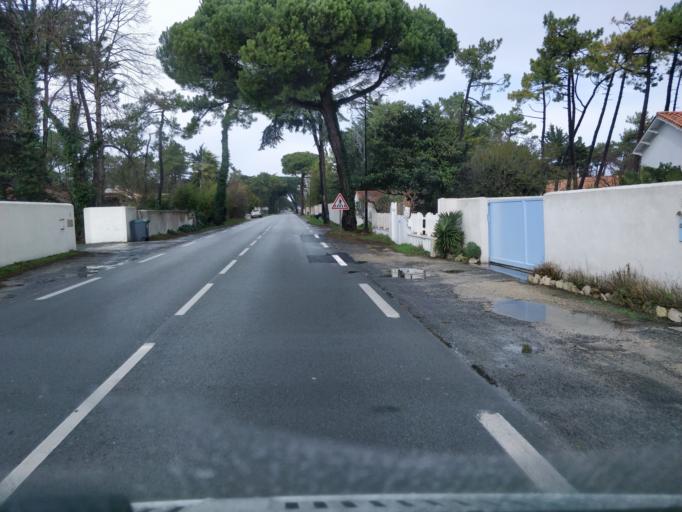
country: FR
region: Poitou-Charentes
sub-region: Departement de la Charente-Maritime
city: Rivedoux-Plage
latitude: 46.1714
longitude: -1.2842
